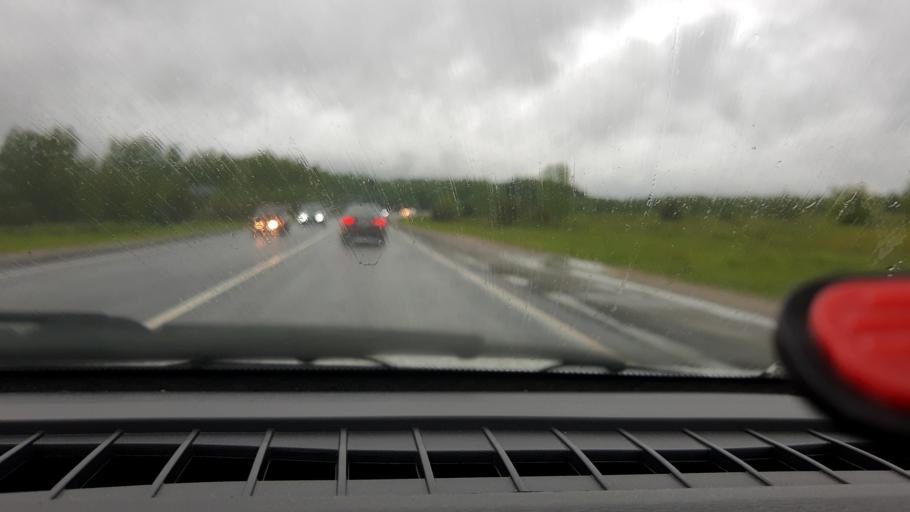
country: RU
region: Nizjnij Novgorod
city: Semenov
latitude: 56.7317
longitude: 44.3031
